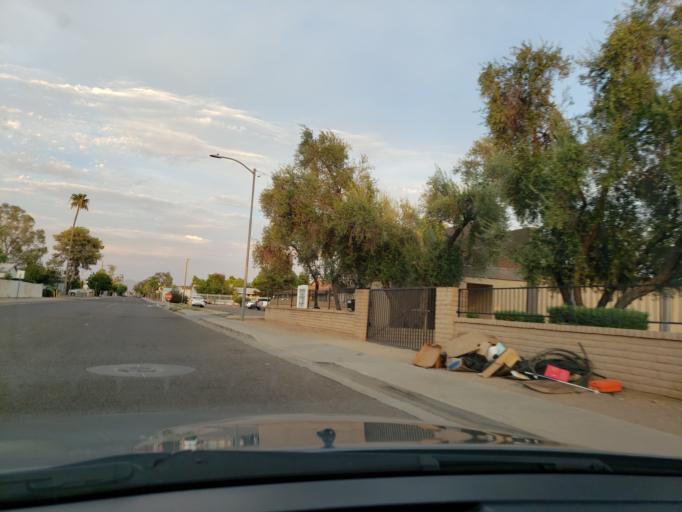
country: US
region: Arizona
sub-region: Maricopa County
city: Paradise Valley
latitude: 33.6353
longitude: -112.0211
